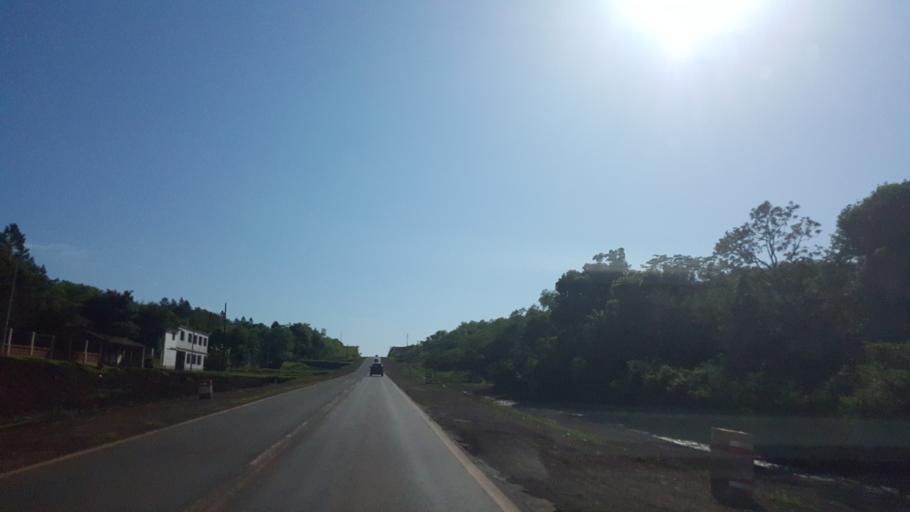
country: AR
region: Misiones
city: Santa Ana
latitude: -27.3734
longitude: -55.5701
